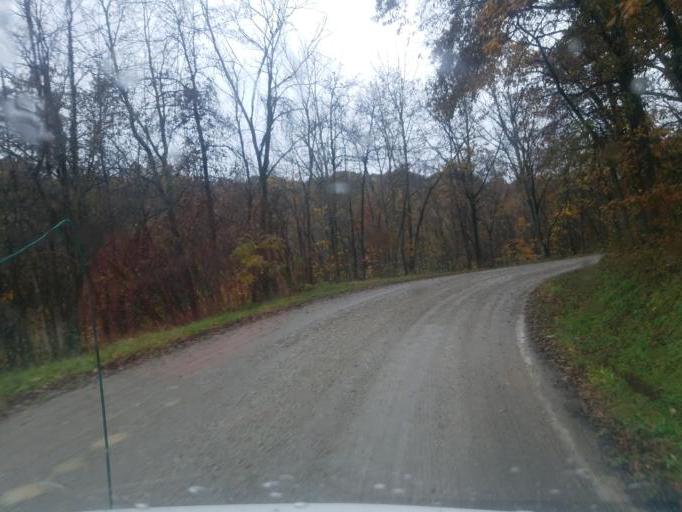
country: US
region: Ohio
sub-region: Washington County
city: Beverly
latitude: 39.4650
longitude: -81.6740
